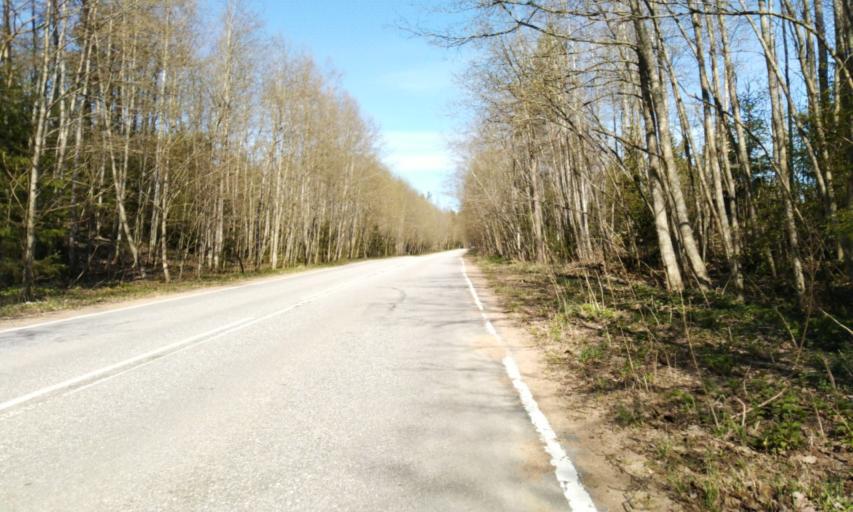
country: RU
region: Leningrad
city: Garbolovo
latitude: 60.4074
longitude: 30.4642
